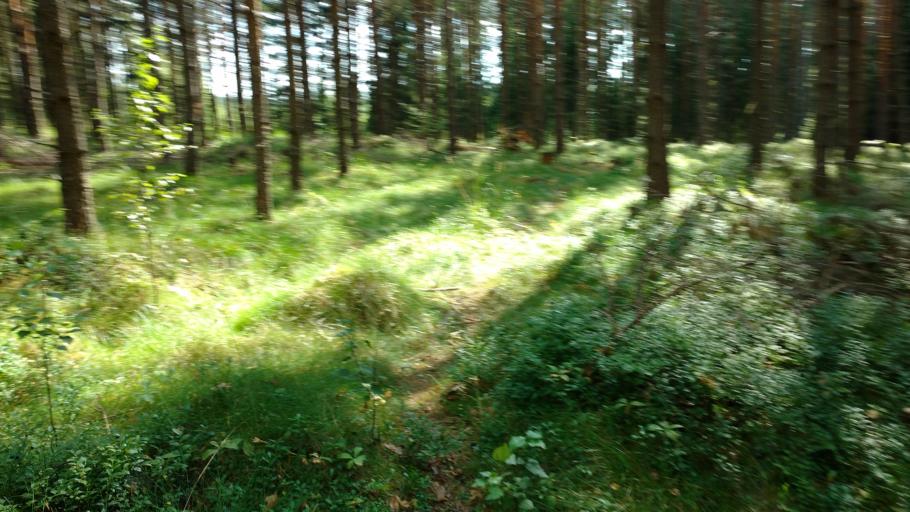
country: FI
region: Varsinais-Suomi
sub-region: Salo
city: Pertteli
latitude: 60.3992
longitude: 23.2169
